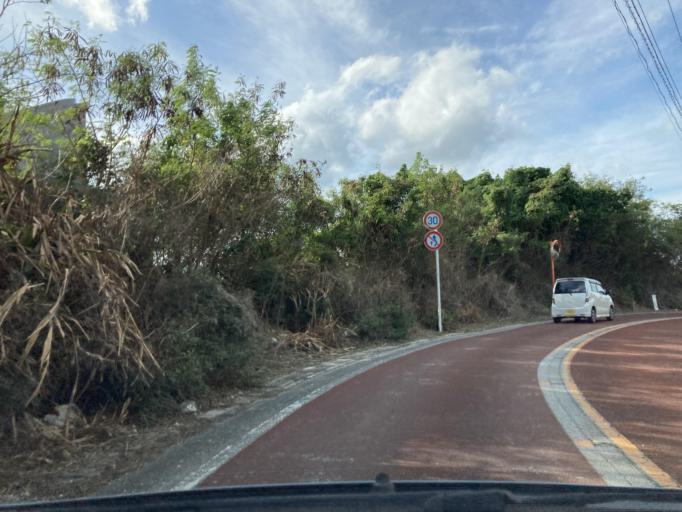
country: JP
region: Okinawa
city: Itoman
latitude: 26.1218
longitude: 127.6781
